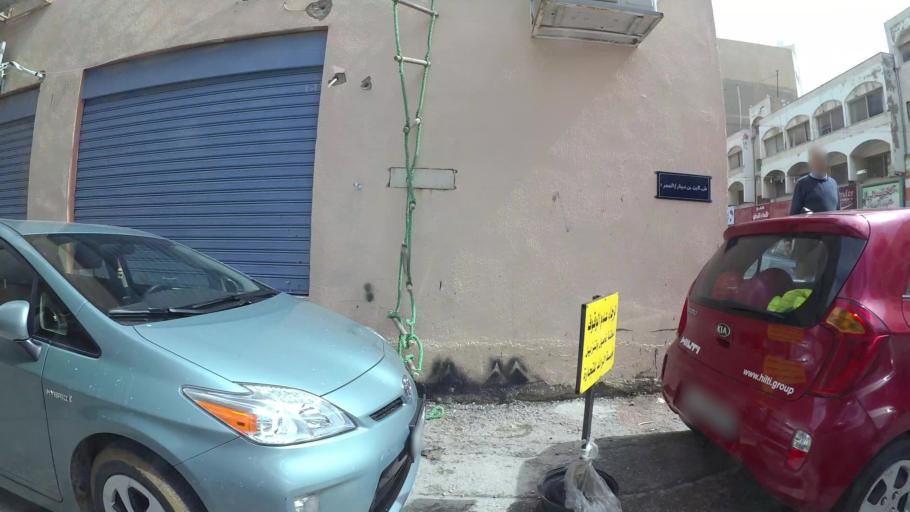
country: JO
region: Amman
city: Al Jubayhah
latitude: 31.9903
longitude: 35.8484
